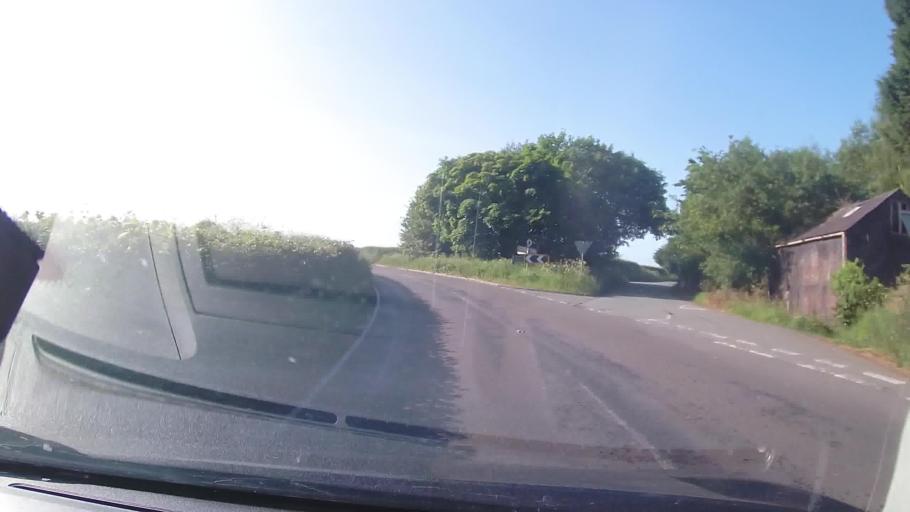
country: GB
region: England
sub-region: Shropshire
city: Shawbury
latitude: 52.7672
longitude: -2.6340
